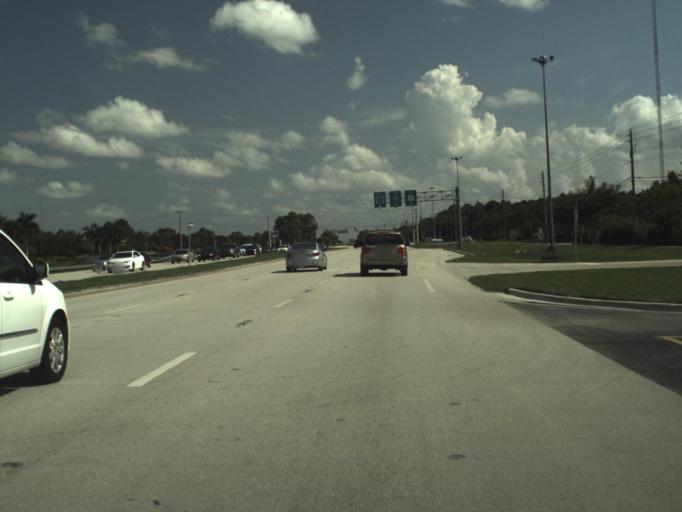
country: US
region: Florida
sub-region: Palm Beach County
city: Wellington
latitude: 26.5950
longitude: -80.2059
